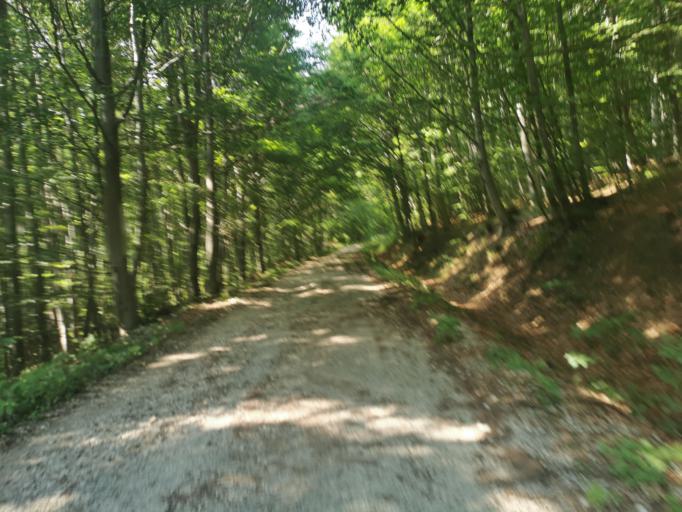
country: SK
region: Trenciansky
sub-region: Okres Myjava
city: Myjava
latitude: 48.8193
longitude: 17.5620
